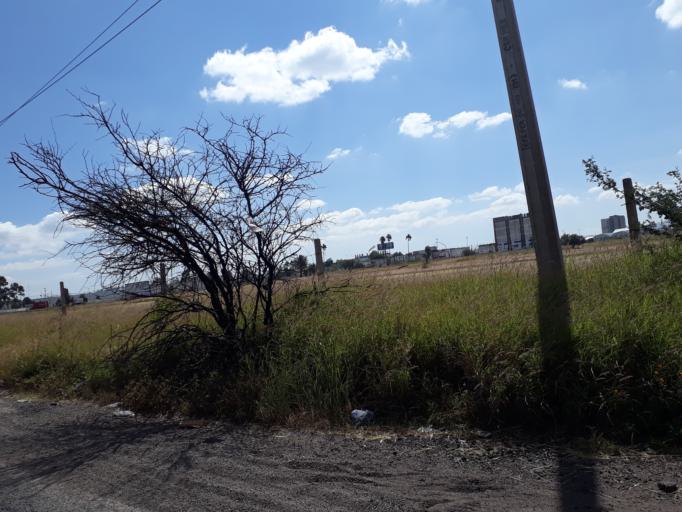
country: MX
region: Aguascalientes
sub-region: Aguascalientes
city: San Sebastian [Fraccionamiento]
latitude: 21.8195
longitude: -102.2899
